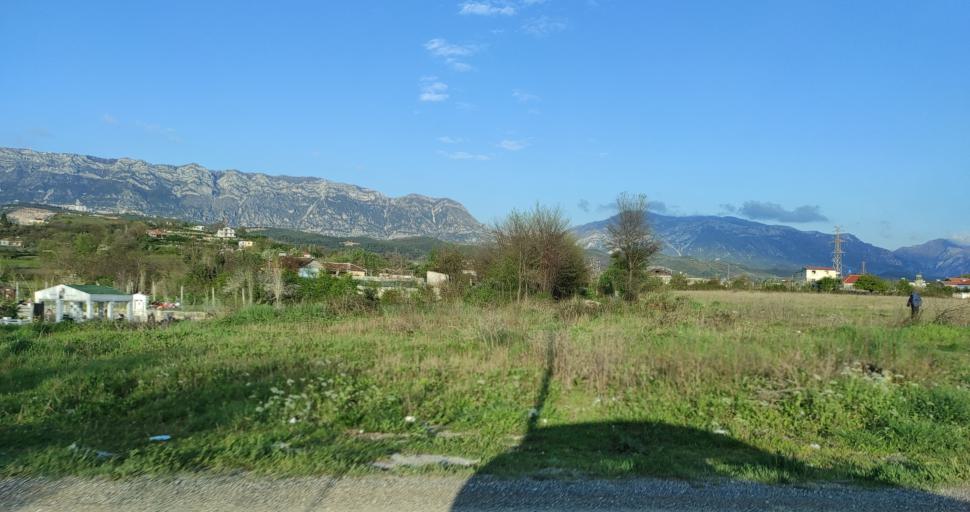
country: AL
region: Durres
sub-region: Rrethi i Krujes
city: Fushe-Kruje
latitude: 41.4820
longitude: 19.7345
